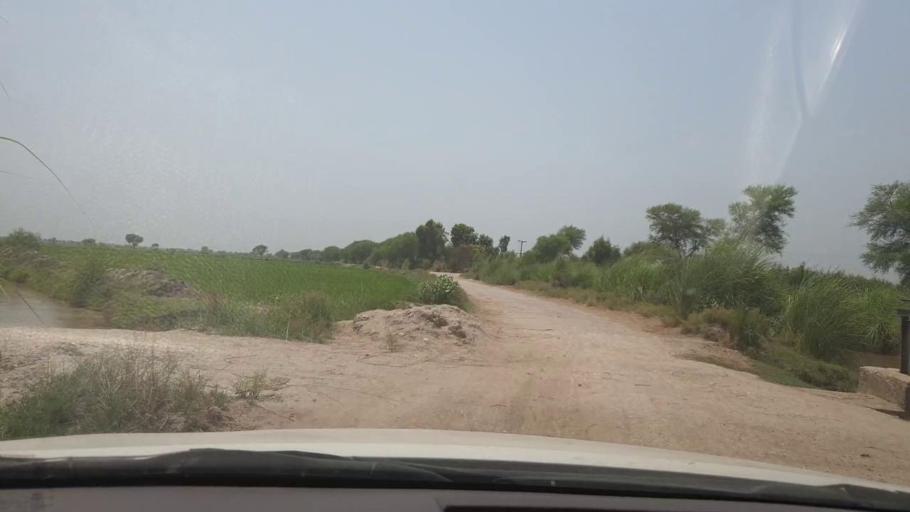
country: PK
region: Sindh
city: Shikarpur
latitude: 28.0845
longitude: 68.5566
